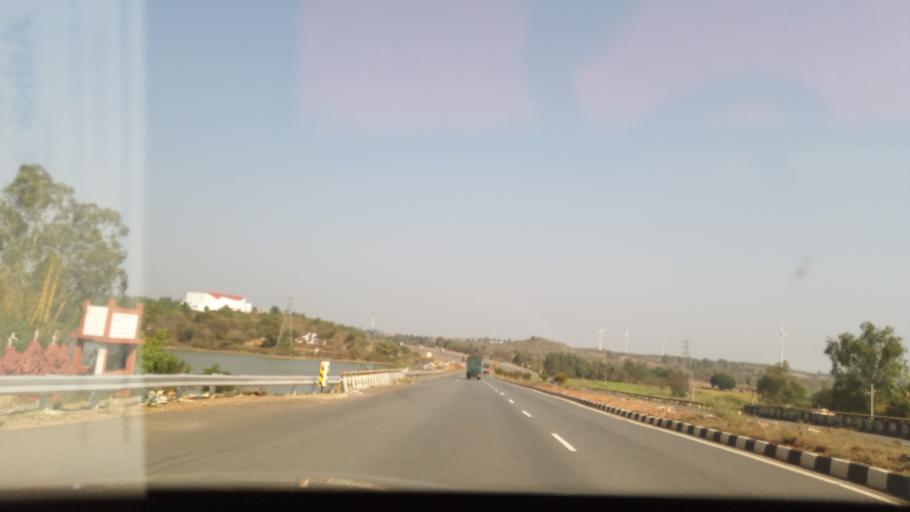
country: IN
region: Karnataka
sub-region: Haveri
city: Shiggaon
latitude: 15.0265
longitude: 75.1814
